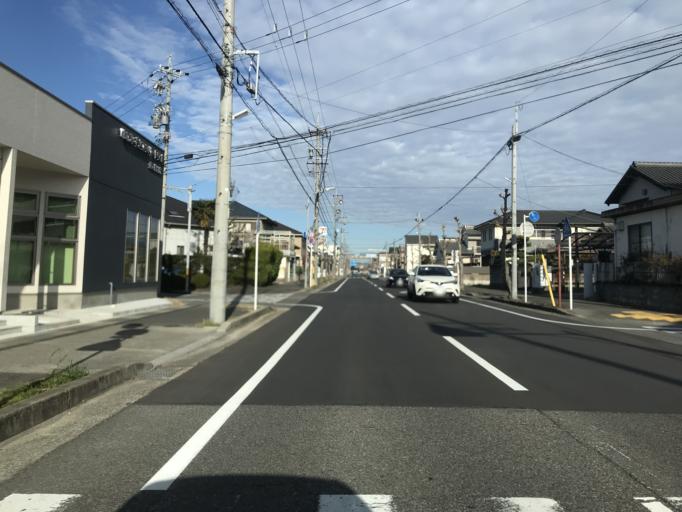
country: JP
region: Aichi
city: Inazawa
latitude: 35.2152
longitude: 136.8350
